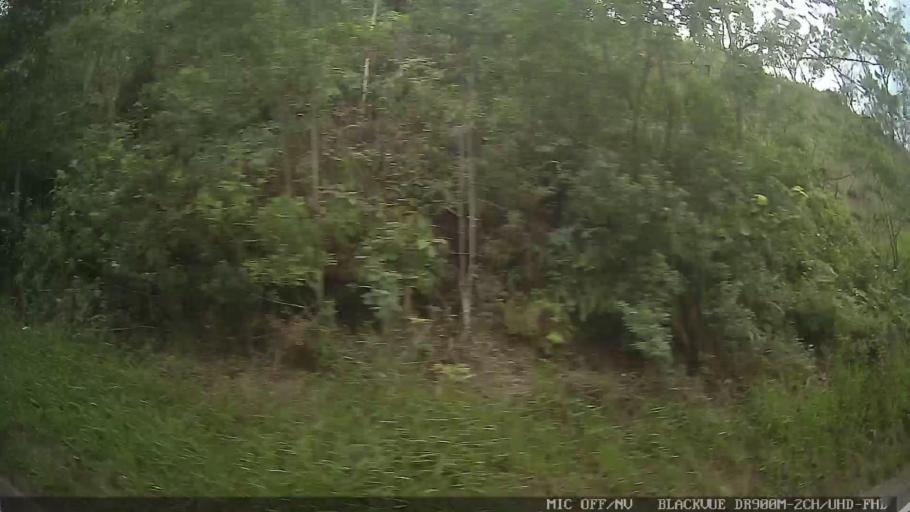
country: BR
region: Sao Paulo
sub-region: Ribeirao Pires
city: Ribeirao Pires
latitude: -23.7277
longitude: -46.4196
